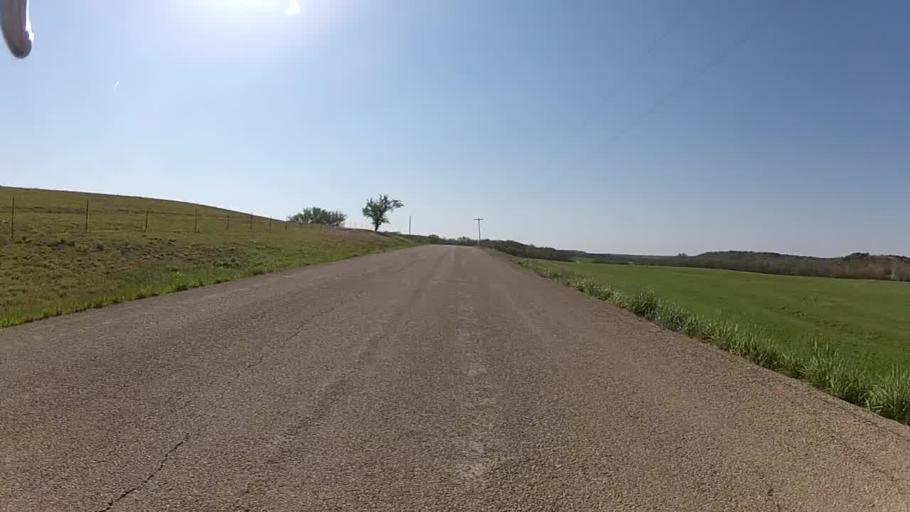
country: US
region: Kansas
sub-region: Riley County
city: Ogden
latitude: 39.0132
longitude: -96.6818
